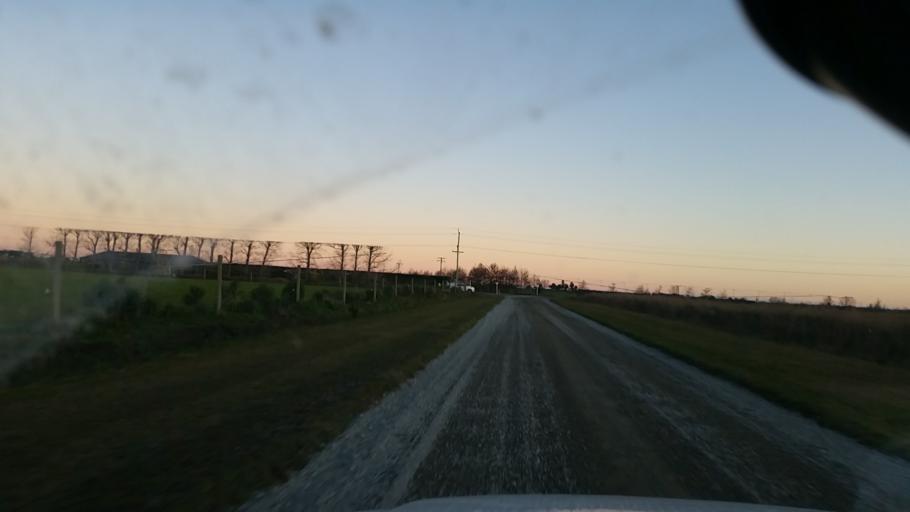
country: NZ
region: Canterbury
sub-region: Ashburton District
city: Tinwald
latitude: -44.0669
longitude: 171.6603
